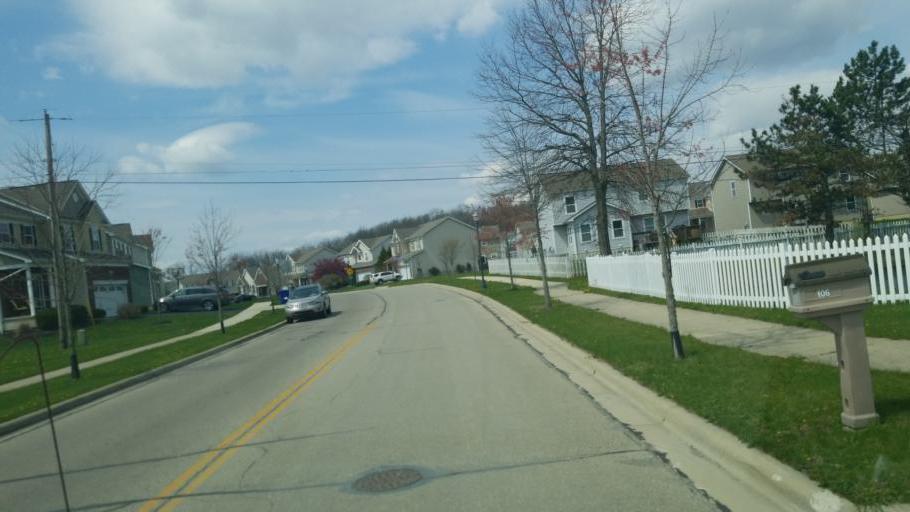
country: US
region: Ohio
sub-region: Delaware County
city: Delaware
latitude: 40.2922
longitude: -83.0901
